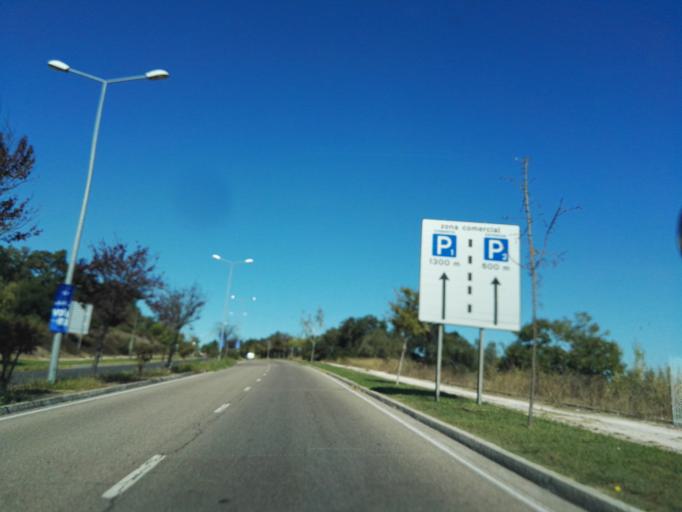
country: PT
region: Setubal
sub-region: Alcochete
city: Alcochete
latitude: 38.7462
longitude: -8.9306
